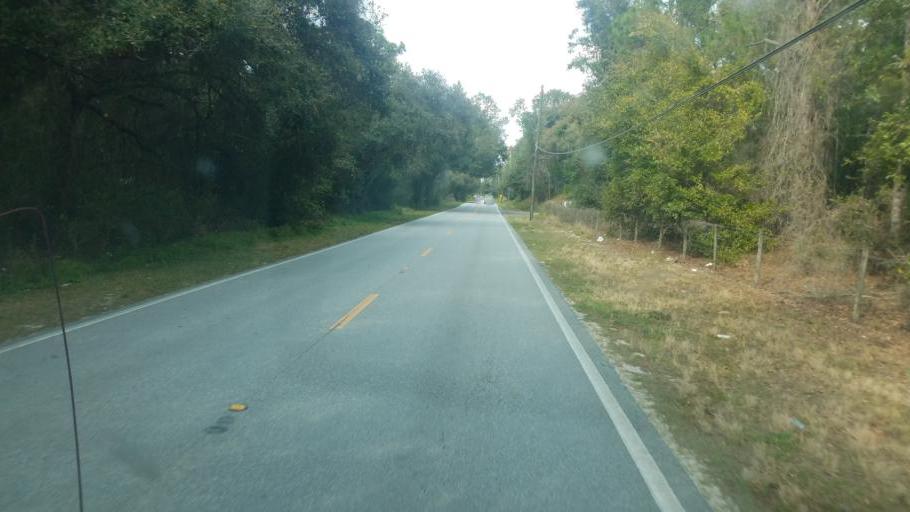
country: US
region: Florida
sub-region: Polk County
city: Davenport
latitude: 28.1893
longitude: -81.5952
